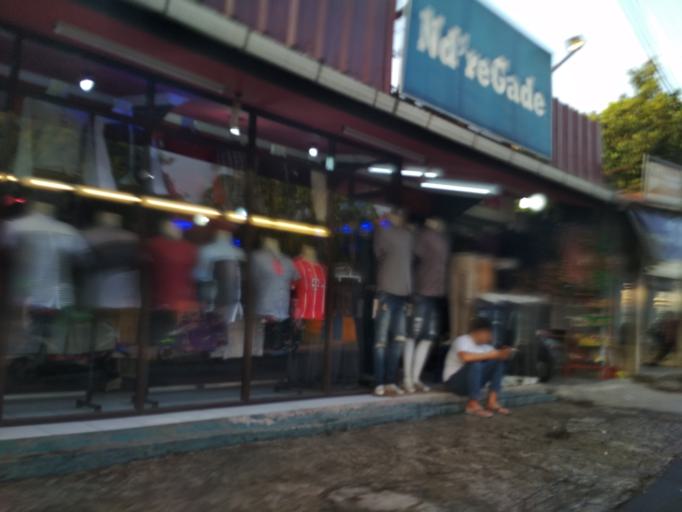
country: ID
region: West Java
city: Ciampea
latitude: -6.5628
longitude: 106.7199
